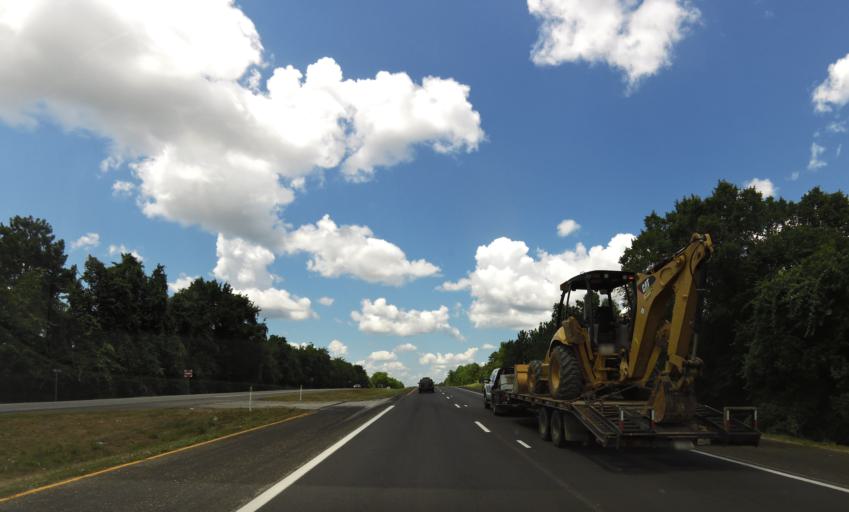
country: US
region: Texas
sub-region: Polk County
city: Livingston
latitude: 30.6287
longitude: -94.9469
